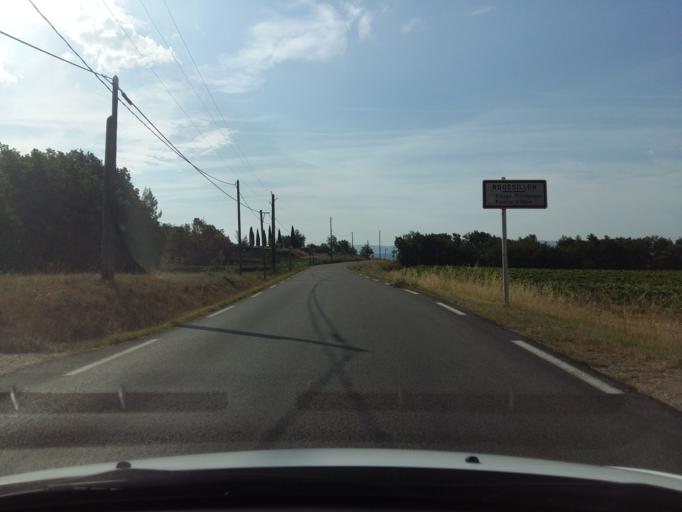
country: FR
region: Provence-Alpes-Cote d'Azur
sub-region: Departement du Vaucluse
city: Roussillon
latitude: 43.9158
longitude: 5.3124
